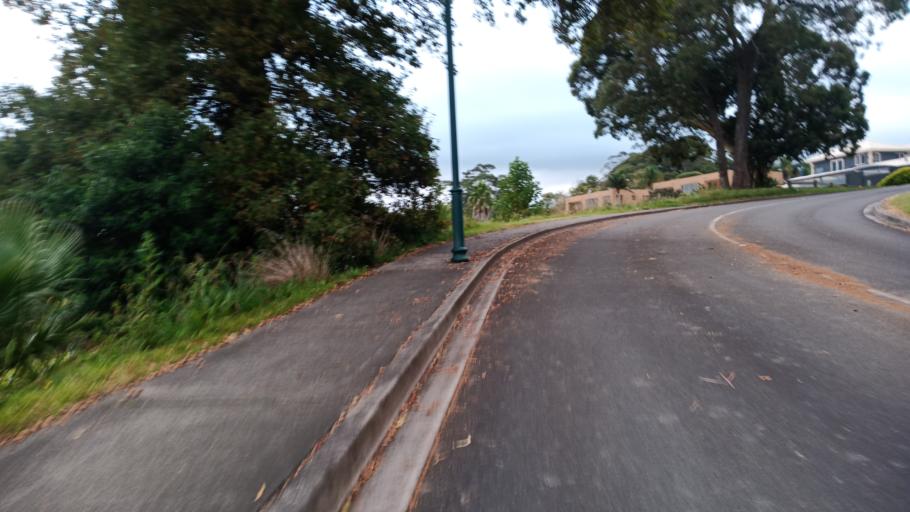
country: NZ
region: Gisborne
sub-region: Gisborne District
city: Gisborne
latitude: -38.6425
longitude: 178.0157
